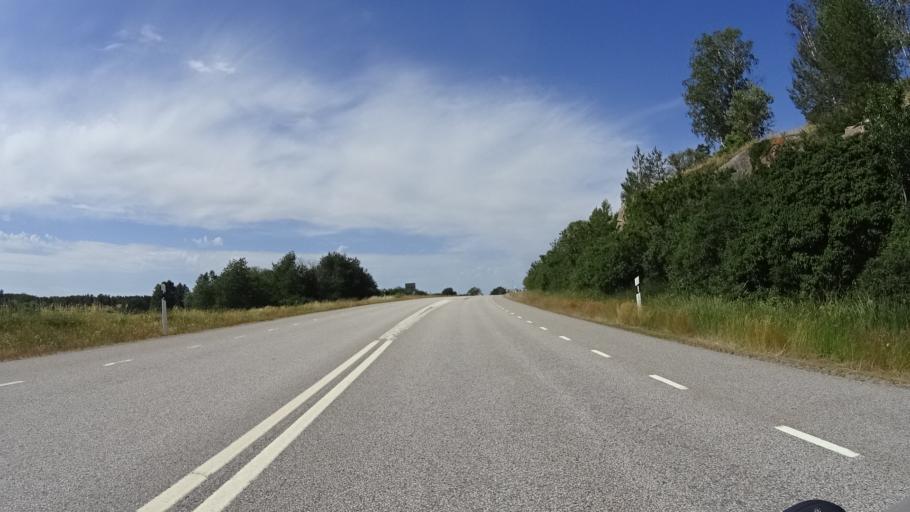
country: SE
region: Kalmar
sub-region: Vasterviks Kommun
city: Gamleby
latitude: 57.9116
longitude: 16.3799
